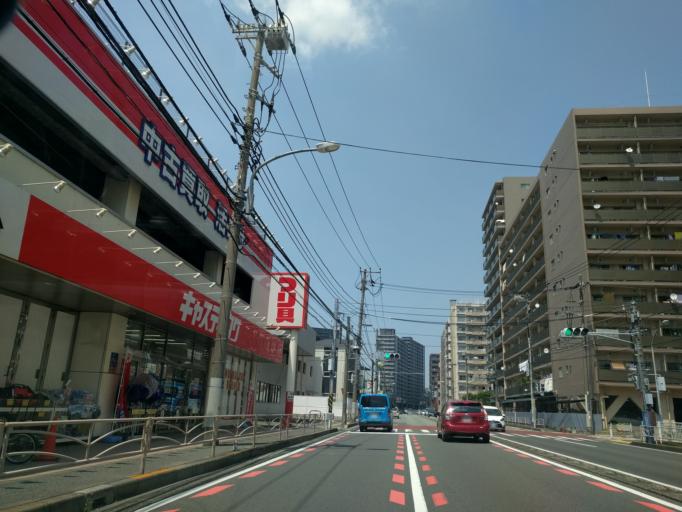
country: JP
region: Kanagawa
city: Yokohama
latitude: 35.3981
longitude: 139.6146
